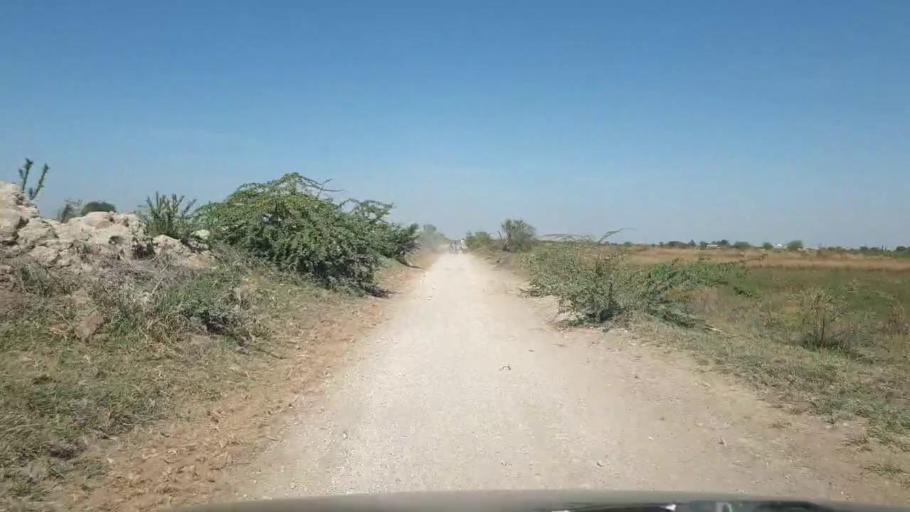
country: PK
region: Sindh
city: Dhoro Naro
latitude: 25.4037
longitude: 69.6140
